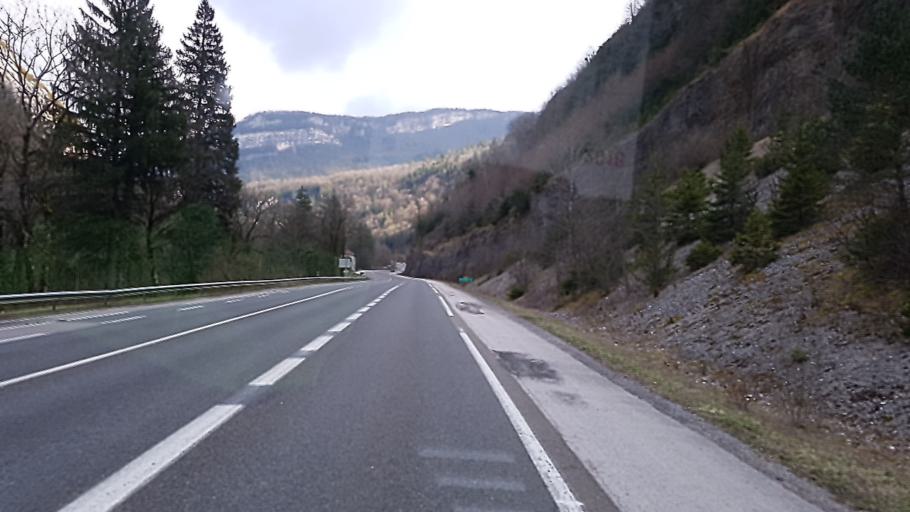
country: FR
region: Franche-Comte
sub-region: Departement du Jura
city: Lavans-les-Saint-Claude
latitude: 46.3806
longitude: 5.8044
